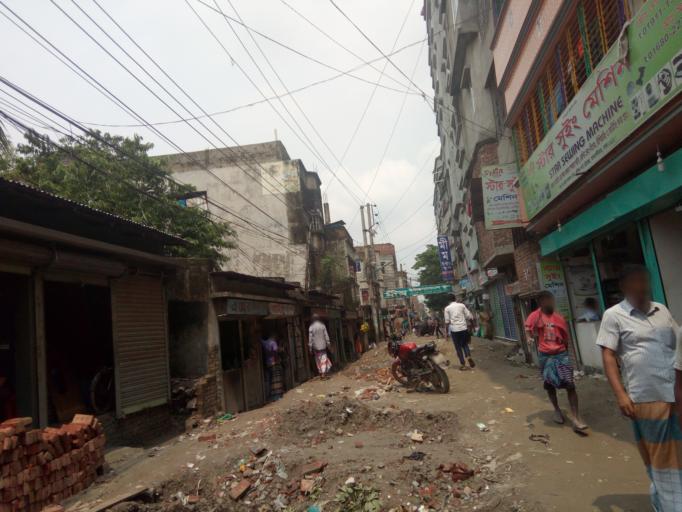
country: BD
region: Dhaka
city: Azimpur
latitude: 23.7184
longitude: 90.3730
